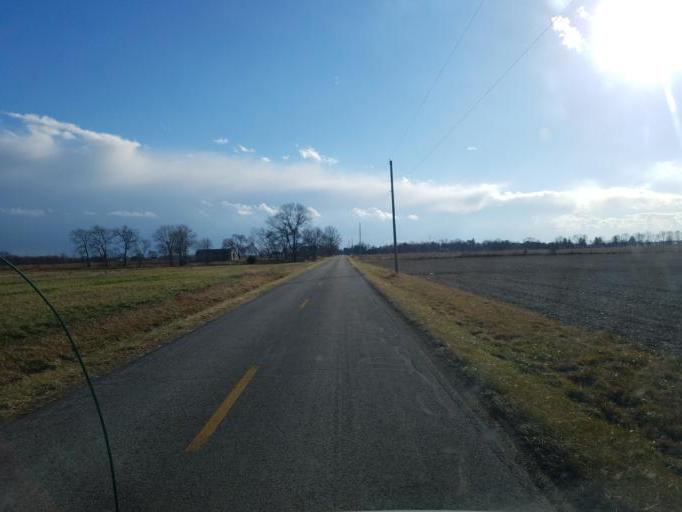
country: US
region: Ohio
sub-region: Marion County
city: Prospect
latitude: 40.3951
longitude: -83.1447
